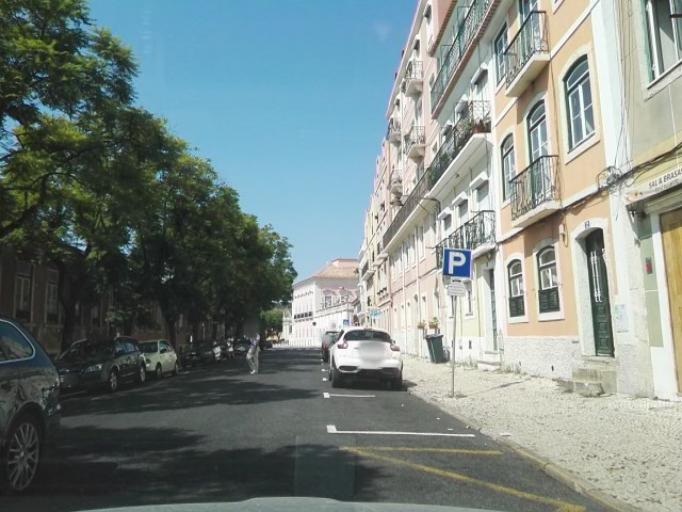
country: PT
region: Setubal
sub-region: Almada
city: Cacilhas
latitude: 38.7057
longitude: -9.1697
